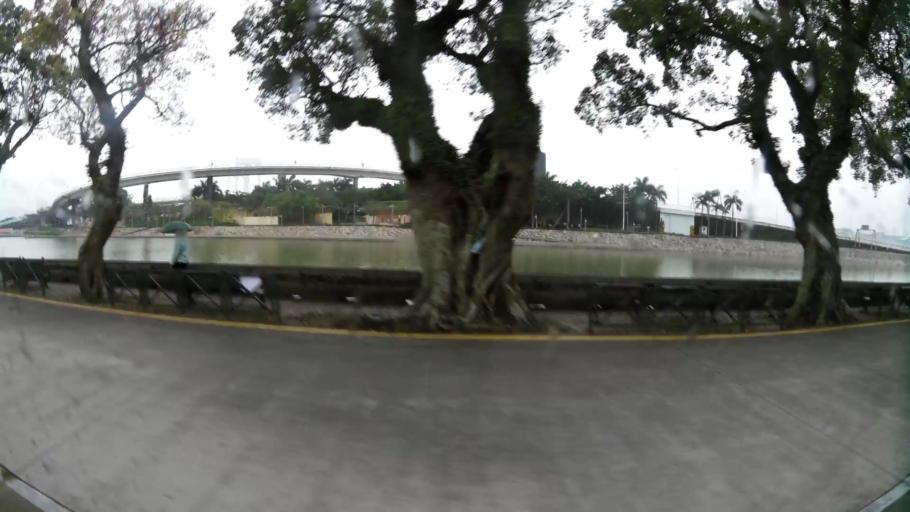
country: CN
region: Guangdong
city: Wanzai
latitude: 22.1815
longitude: 113.5324
